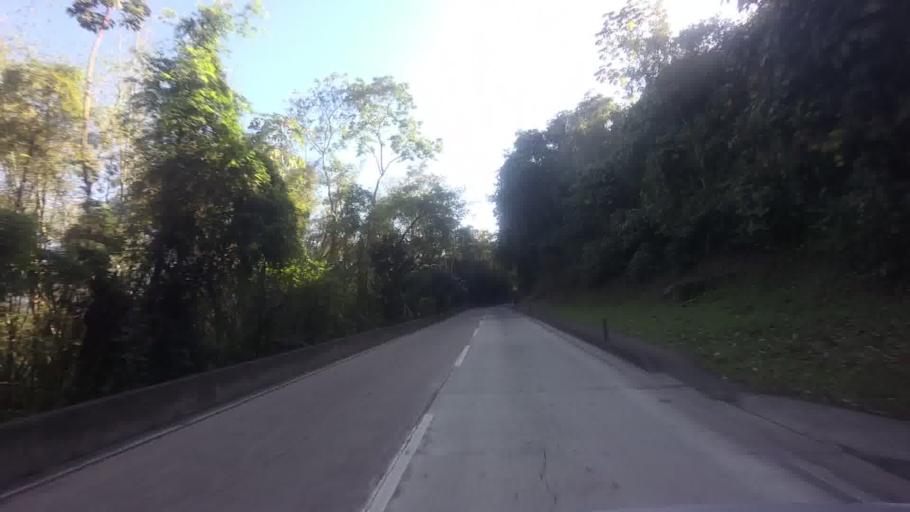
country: BR
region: Rio de Janeiro
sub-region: Petropolis
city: Petropolis
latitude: -22.5989
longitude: -43.2802
